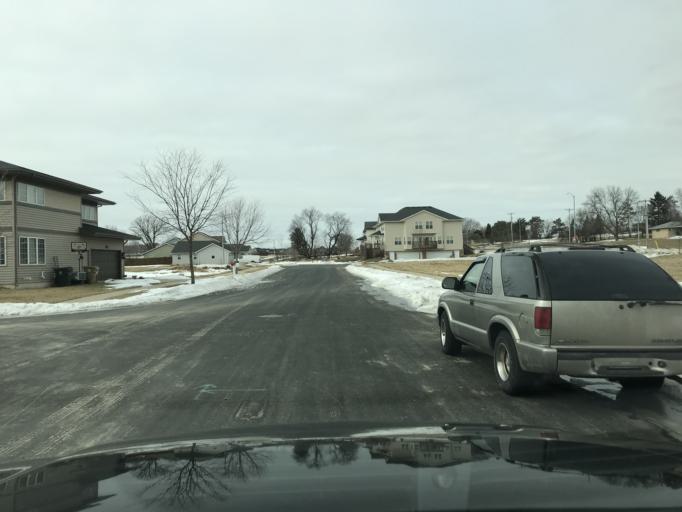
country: US
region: Wisconsin
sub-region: Dane County
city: Cottage Grove
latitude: 43.0990
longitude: -89.2692
